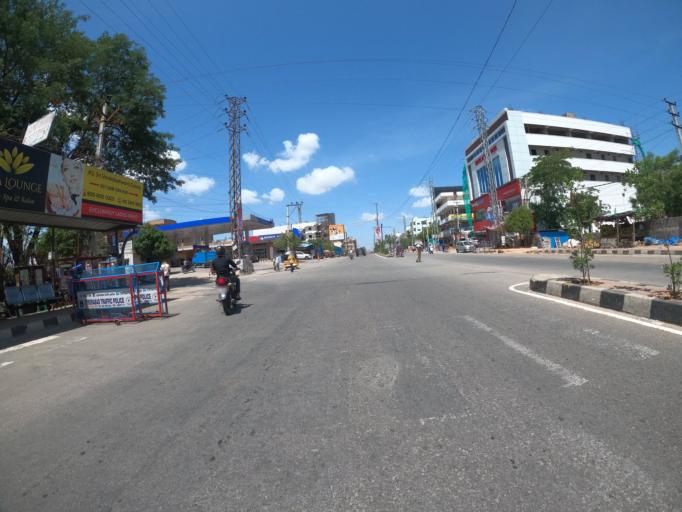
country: IN
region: Telangana
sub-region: Hyderabad
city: Hyderabad
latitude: 17.3596
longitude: 78.3880
